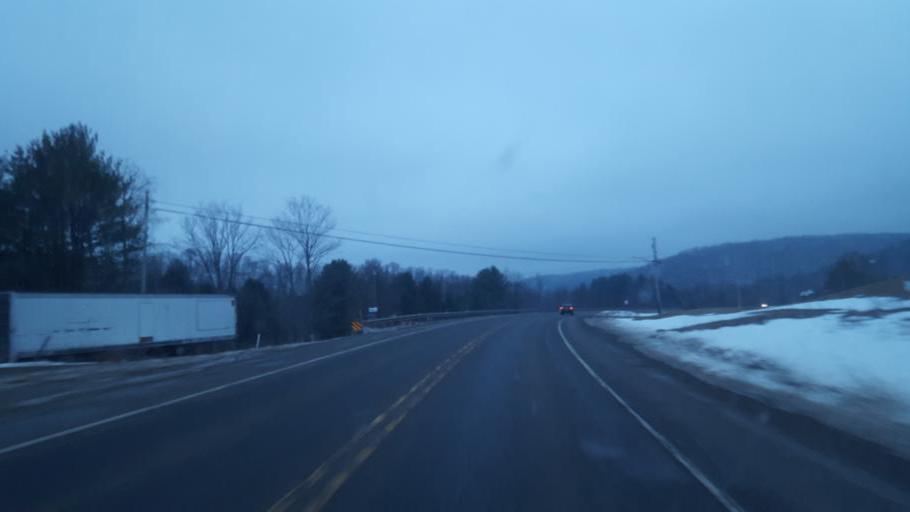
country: US
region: Pennsylvania
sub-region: Potter County
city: Coudersport
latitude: 41.7674
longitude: -78.1249
